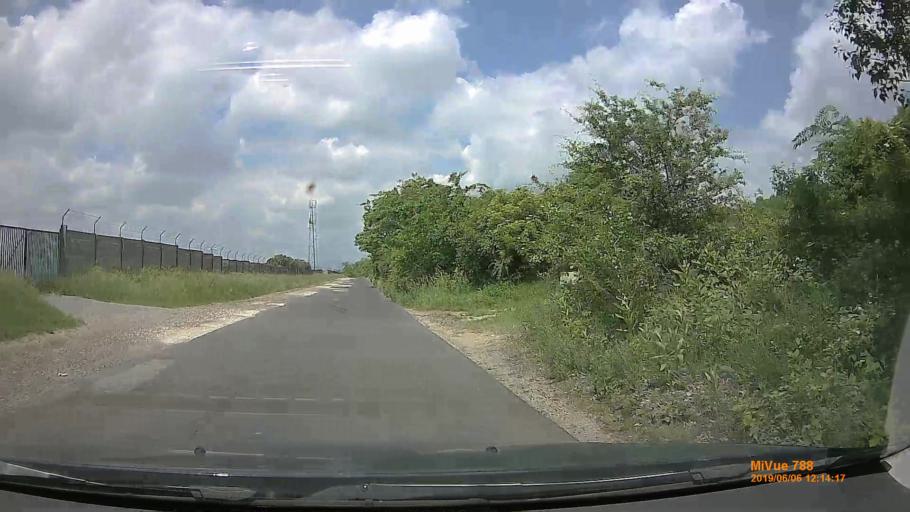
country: HU
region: Pest
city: Mogyorod
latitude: 47.5856
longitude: 19.2572
